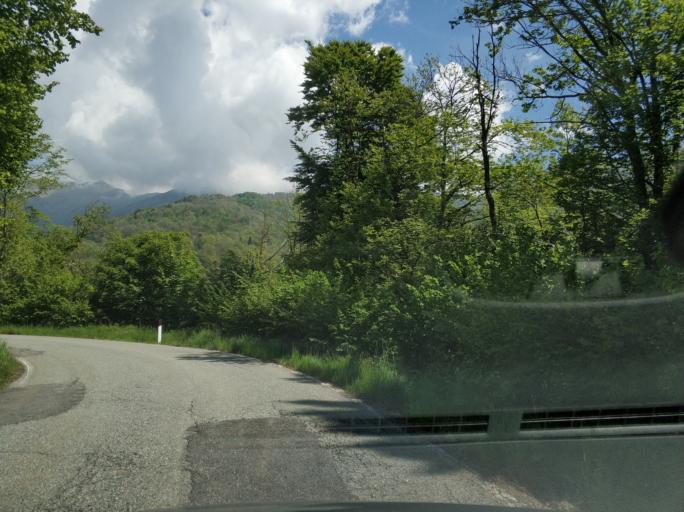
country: IT
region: Piedmont
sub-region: Provincia di Torino
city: Coassolo
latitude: 45.3121
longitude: 7.4709
